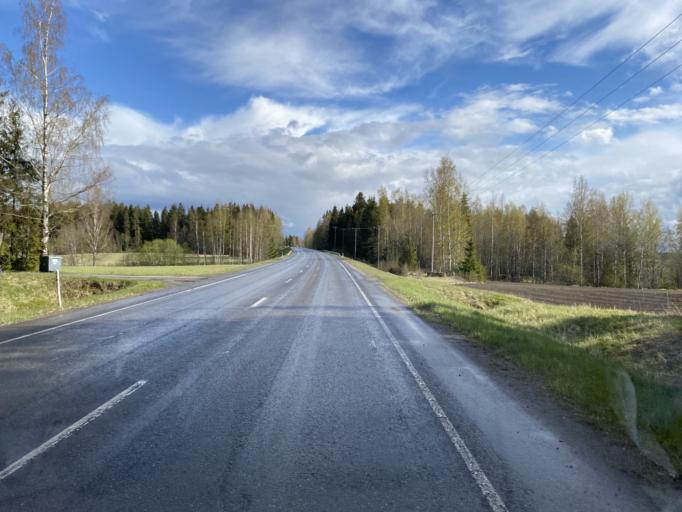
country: FI
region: Pirkanmaa
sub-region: Etelae-Pirkanmaa
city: Viiala
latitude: 61.2403
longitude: 23.7387
